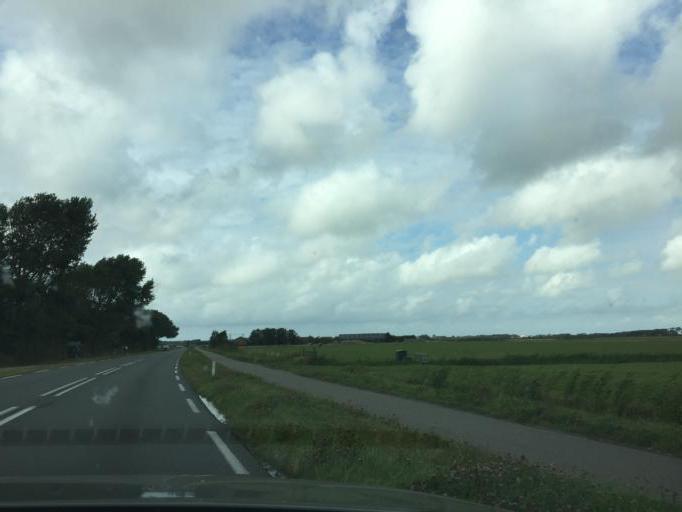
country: NL
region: North Holland
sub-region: Gemeente Texel
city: Den Burg
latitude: 53.0705
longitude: 4.7731
